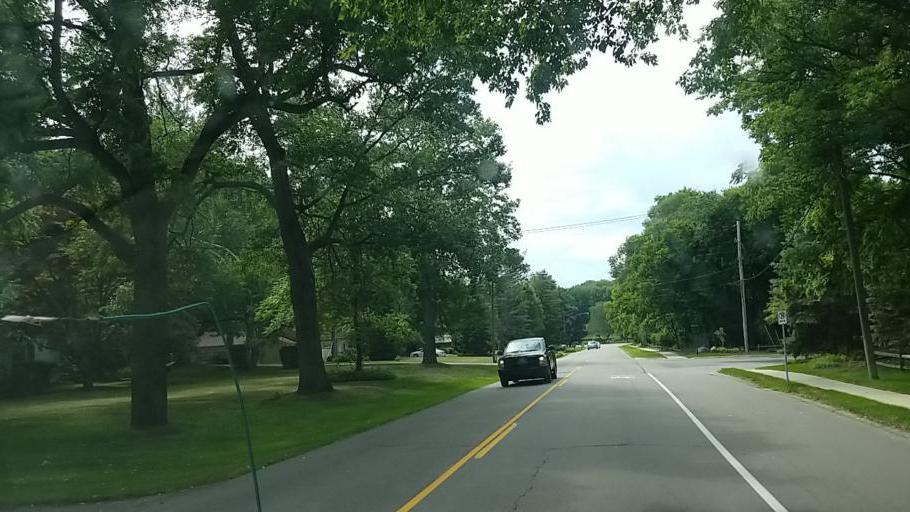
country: US
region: Michigan
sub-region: Kent County
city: Walker
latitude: 42.9933
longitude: -85.7242
